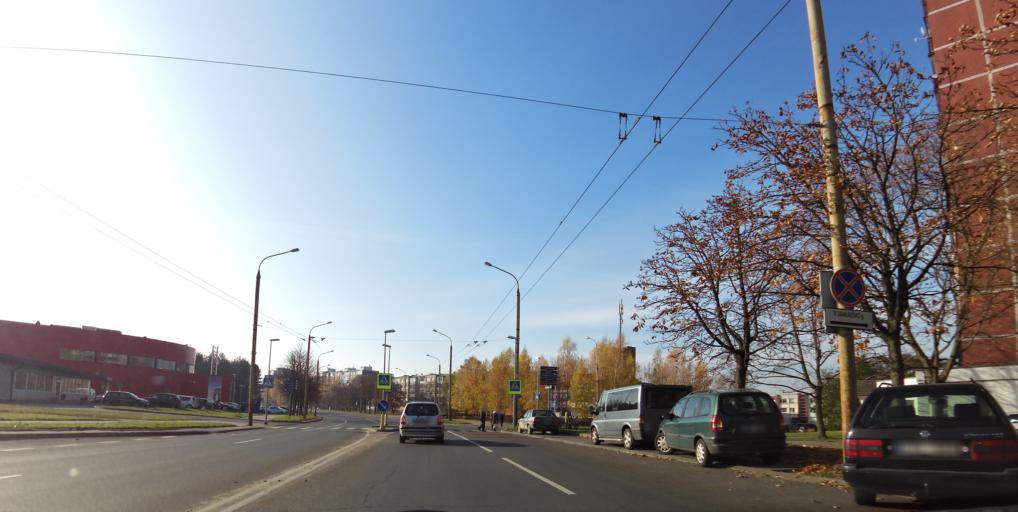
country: LT
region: Vilnius County
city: Lazdynai
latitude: 54.6903
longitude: 25.2104
